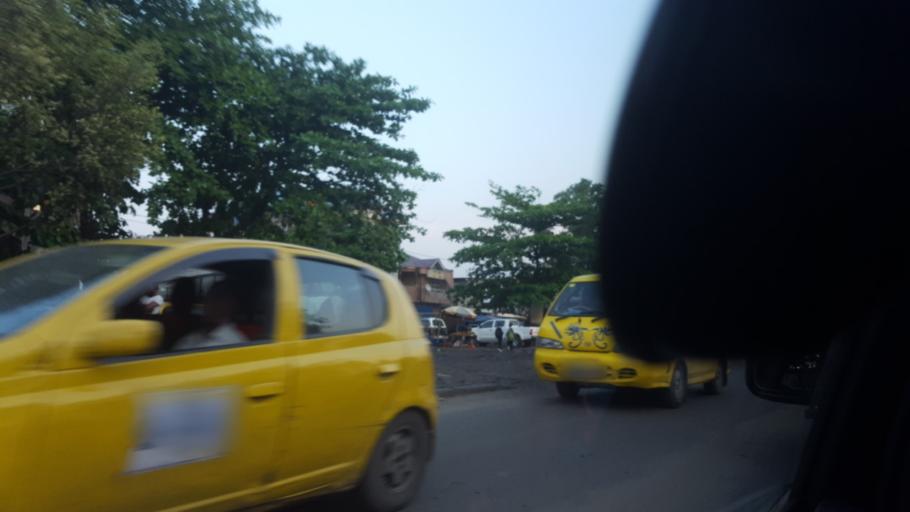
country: CD
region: Kinshasa
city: Kinshasa
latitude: -4.3479
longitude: 15.3249
